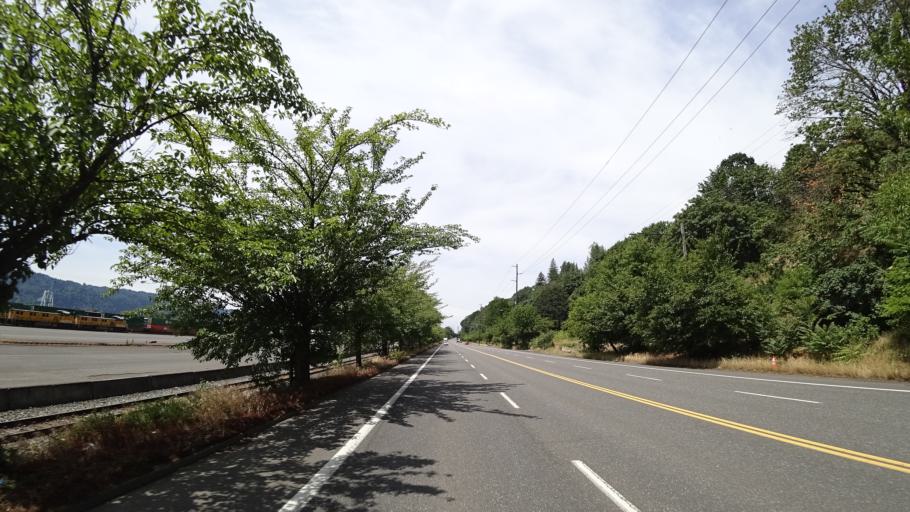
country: US
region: Oregon
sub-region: Multnomah County
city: Portland
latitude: 45.5478
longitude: -122.6843
